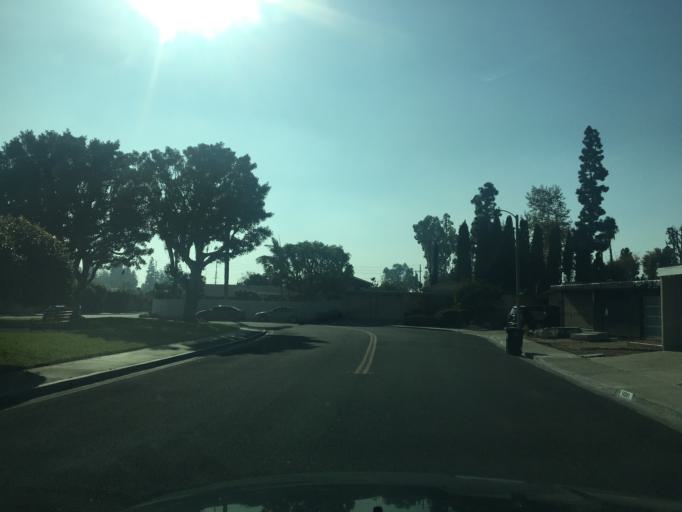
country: US
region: California
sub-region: Orange County
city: Tustin
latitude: 33.7323
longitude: -117.8224
